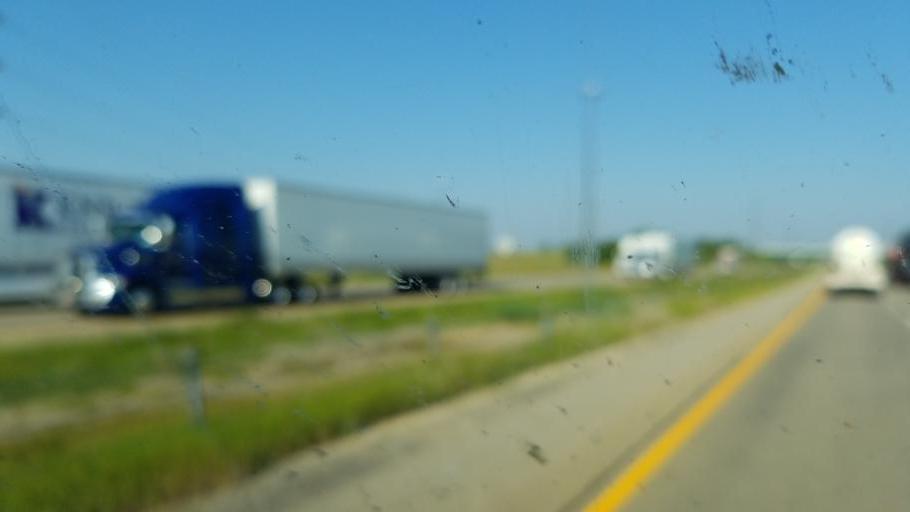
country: US
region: Illinois
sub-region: LaSalle County
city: Deer Park
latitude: 41.3677
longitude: -89.0055
